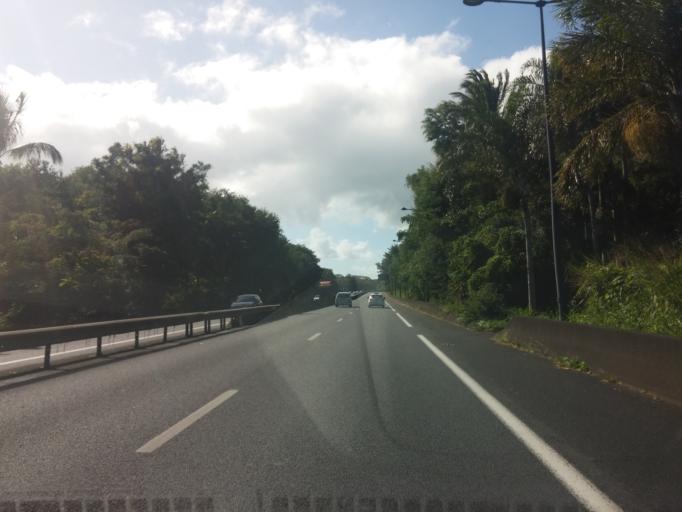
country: RE
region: Reunion
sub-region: Reunion
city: Saint-Denis
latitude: -20.8865
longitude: 55.4928
